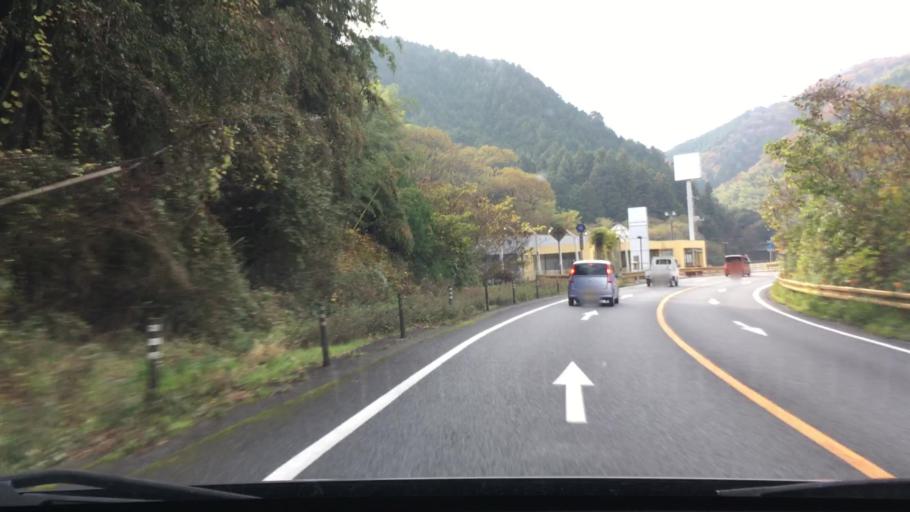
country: JP
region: Yamaguchi
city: Iwakuni
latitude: 34.1292
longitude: 132.1447
